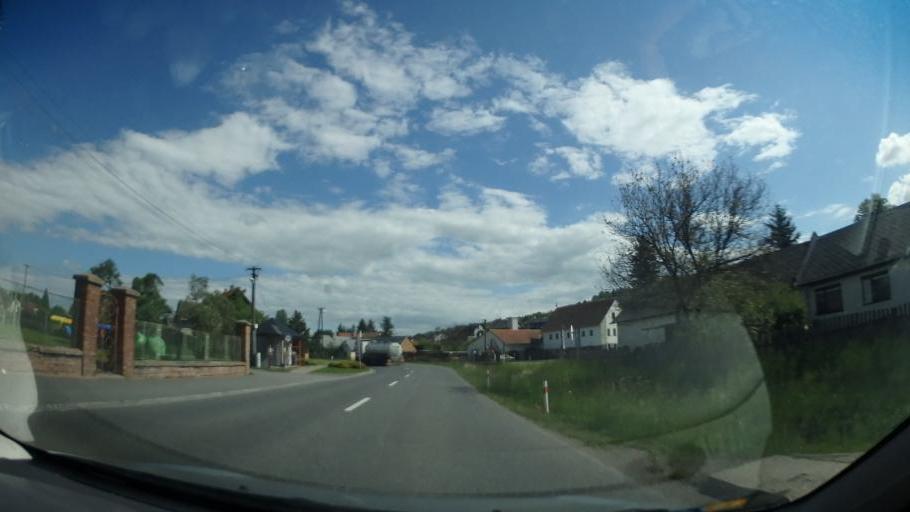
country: CZ
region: Pardubicky
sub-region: Okres Svitavy
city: Moravska Trebova
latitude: 49.7305
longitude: 16.6431
